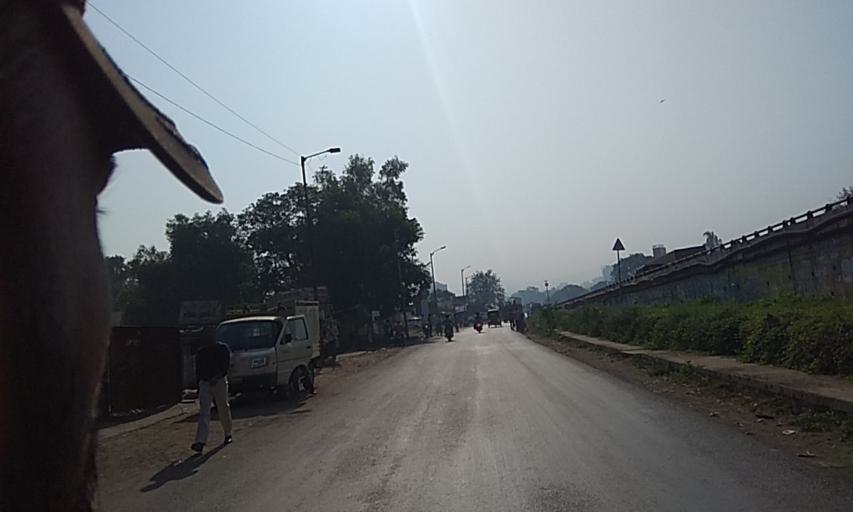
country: IN
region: Maharashtra
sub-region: Pune Division
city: Kharakvasla
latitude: 18.4785
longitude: 73.8061
